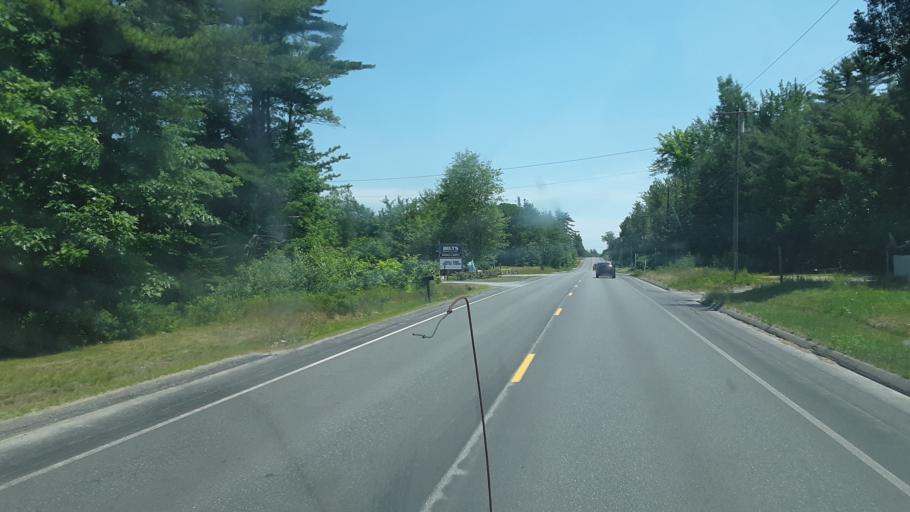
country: US
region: Maine
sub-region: Hancock County
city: Hancock
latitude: 44.5265
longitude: -68.2471
